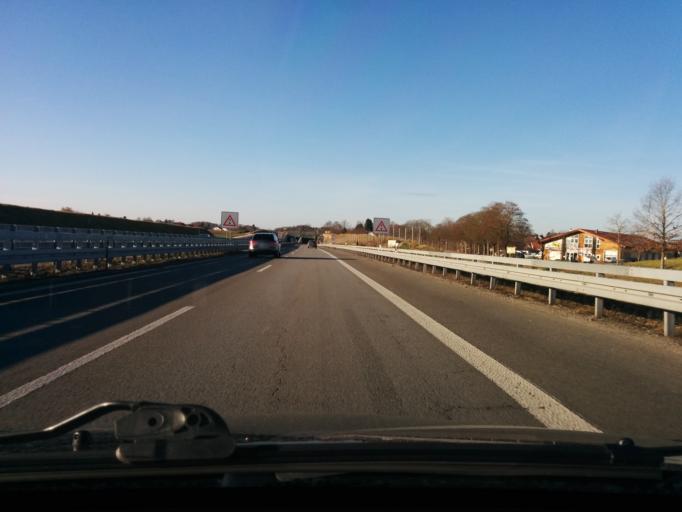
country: DE
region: Bavaria
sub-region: Upper Bavaria
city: Worthsee
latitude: 48.0862
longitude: 11.2106
